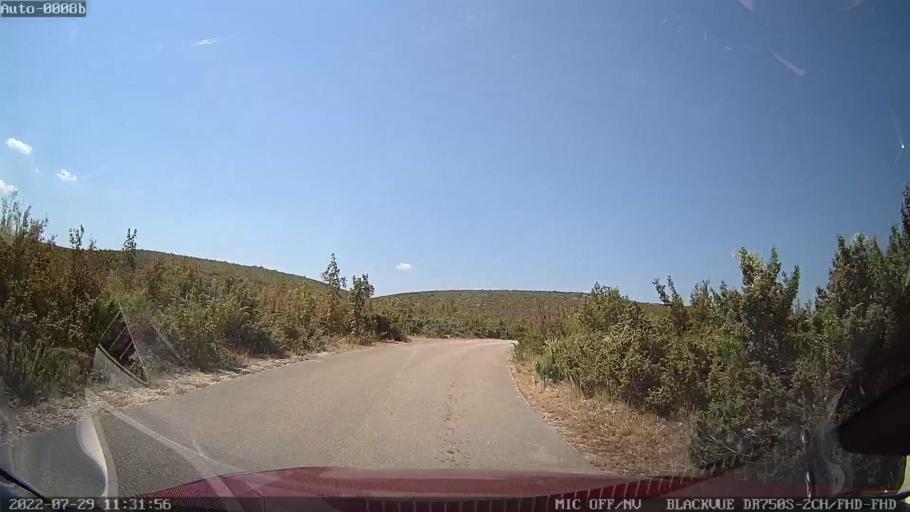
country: HR
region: Zadarska
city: Obrovac
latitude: 44.1935
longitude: 15.7438
